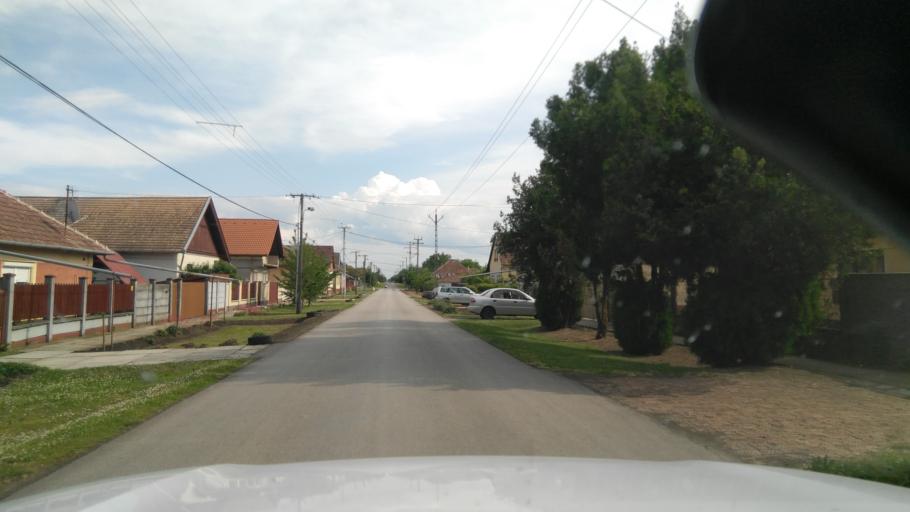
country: HU
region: Bekes
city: Ujkigyos
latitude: 46.5896
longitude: 21.0338
